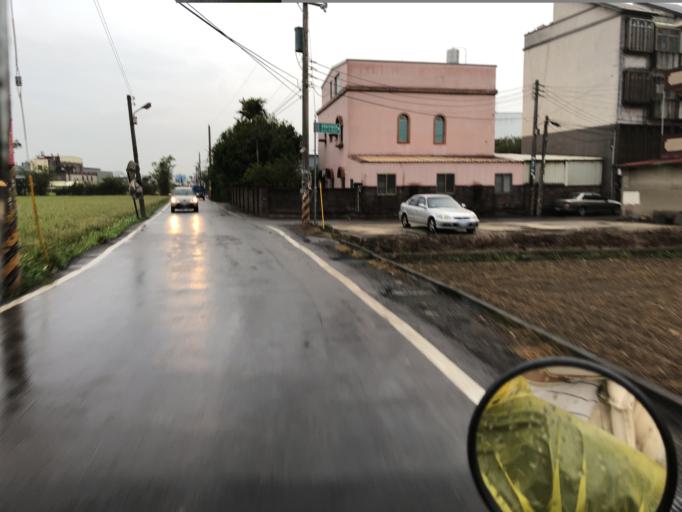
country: TW
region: Taiwan
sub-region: Hsinchu
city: Zhubei
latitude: 24.8460
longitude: 120.9874
